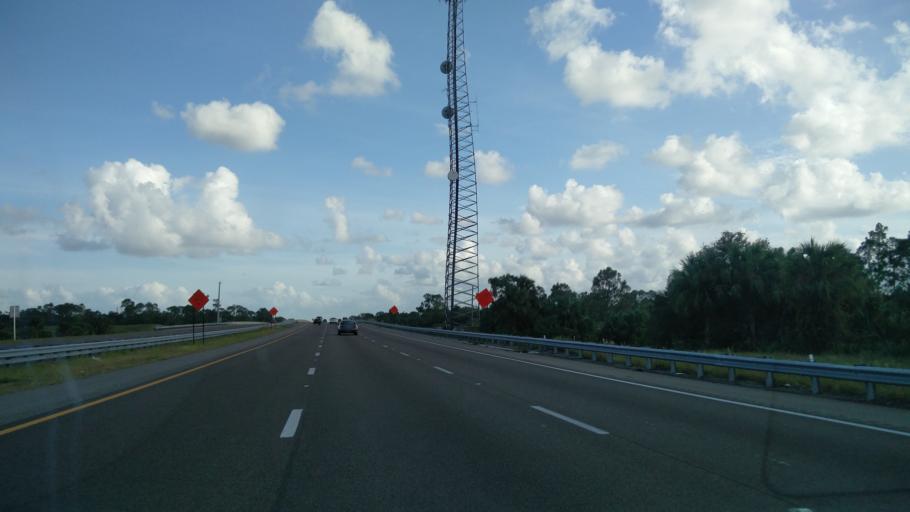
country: US
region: Florida
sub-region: Indian River County
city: Roseland
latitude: 27.8293
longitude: -80.5613
